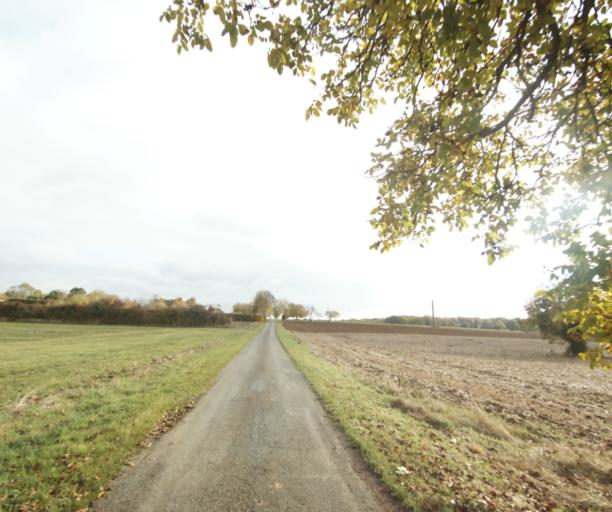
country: FR
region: Poitou-Charentes
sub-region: Departement de la Charente-Maritime
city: Saint-Georges-des-Coteaux
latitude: 45.7675
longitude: -0.6868
